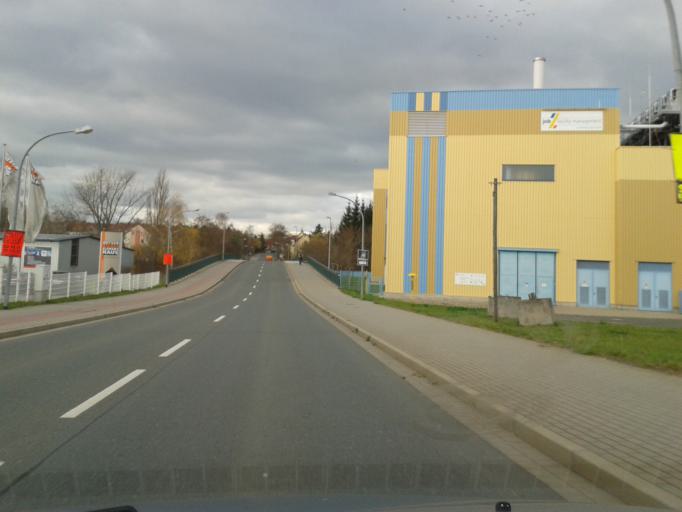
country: DE
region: Thuringia
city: Hermsdorf
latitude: 50.9001
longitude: 11.8525
